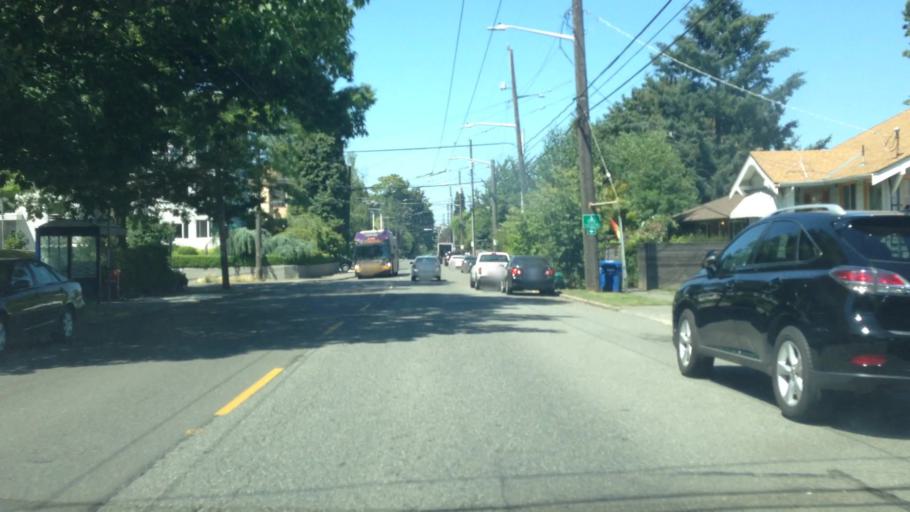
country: US
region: Washington
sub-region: King County
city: Seattle
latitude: 47.5879
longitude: -122.3149
